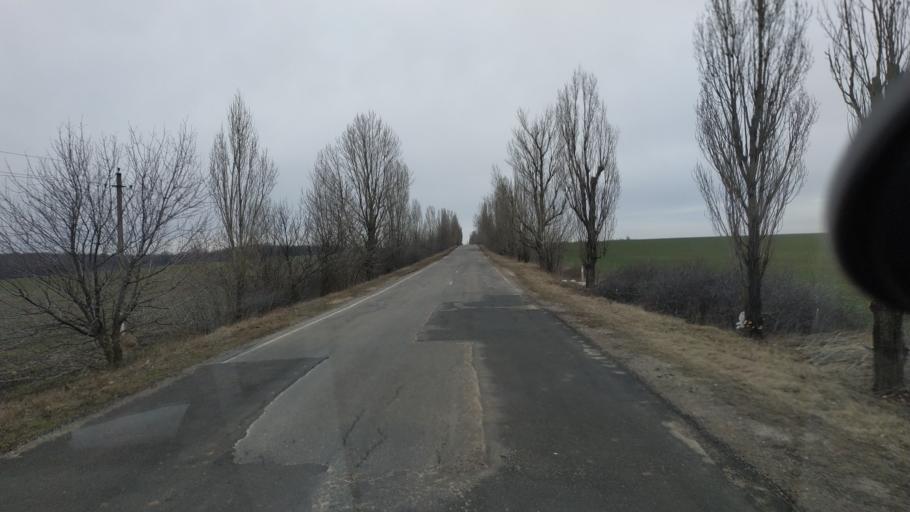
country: MD
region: Telenesti
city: Cocieri
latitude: 47.3733
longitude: 29.0431
